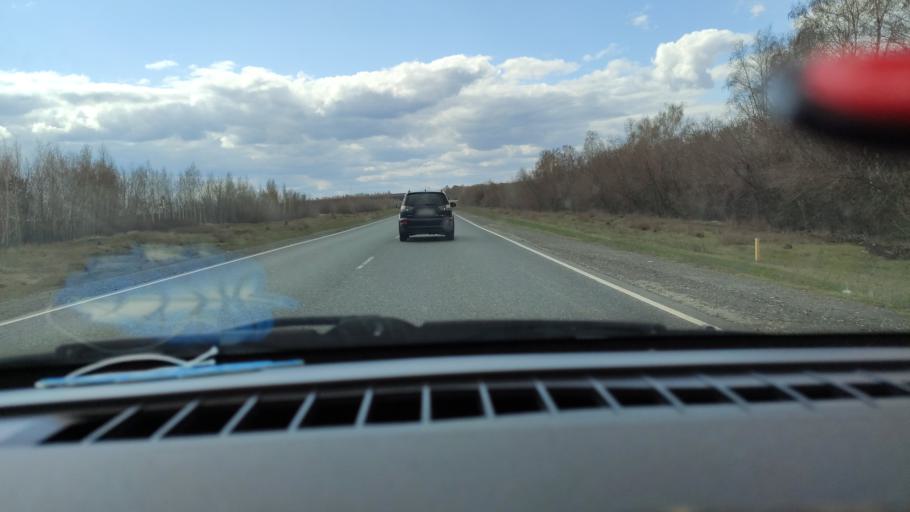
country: RU
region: Saratov
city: Balakovo
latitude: 52.1373
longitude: 47.7972
